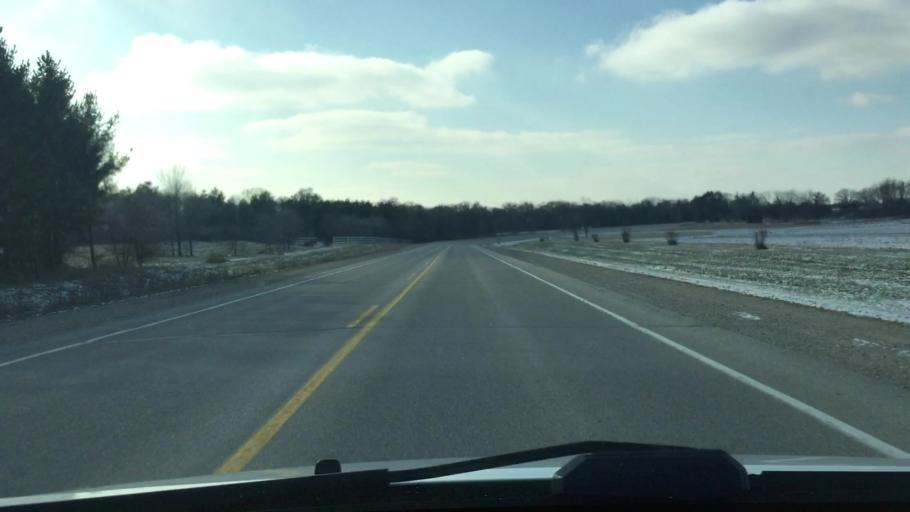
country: US
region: Wisconsin
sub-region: Waukesha County
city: North Prairie
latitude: 42.9182
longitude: -88.4371
